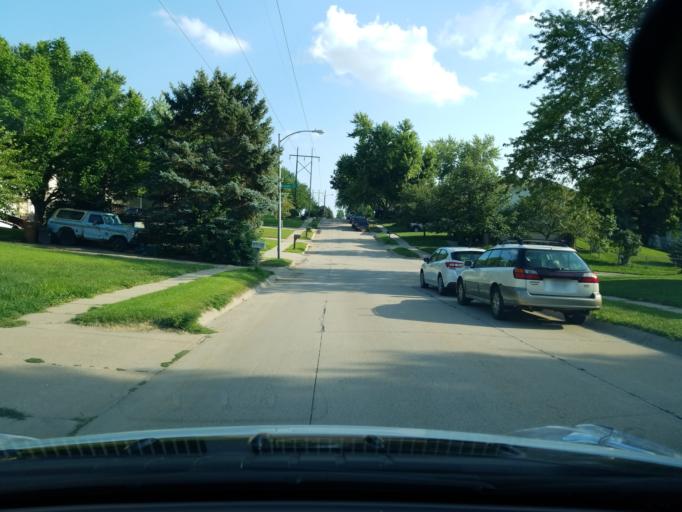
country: US
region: Nebraska
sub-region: Sarpy County
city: Offutt Air Force Base
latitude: 41.1313
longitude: -95.9619
